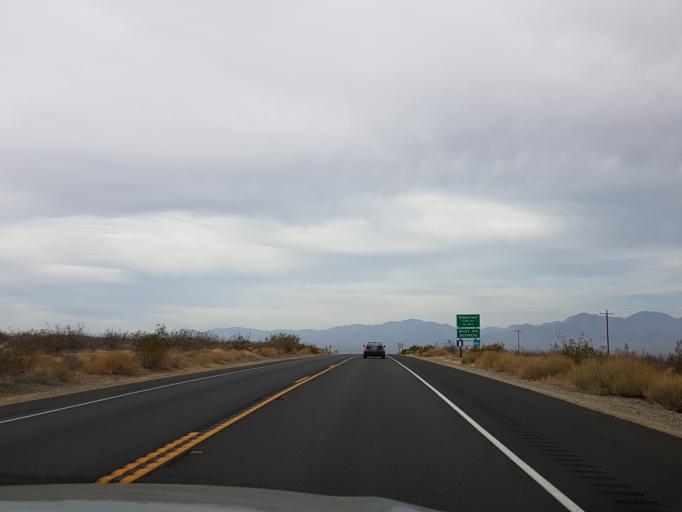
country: US
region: California
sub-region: Kern County
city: Ridgecrest
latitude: 35.5475
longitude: -117.7045
